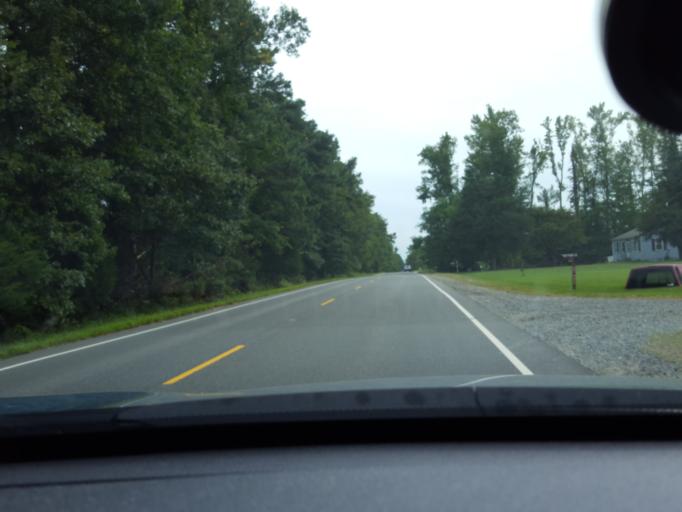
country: US
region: Virginia
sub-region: Caroline County
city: Bowling Green
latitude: 37.9886
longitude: -77.3377
